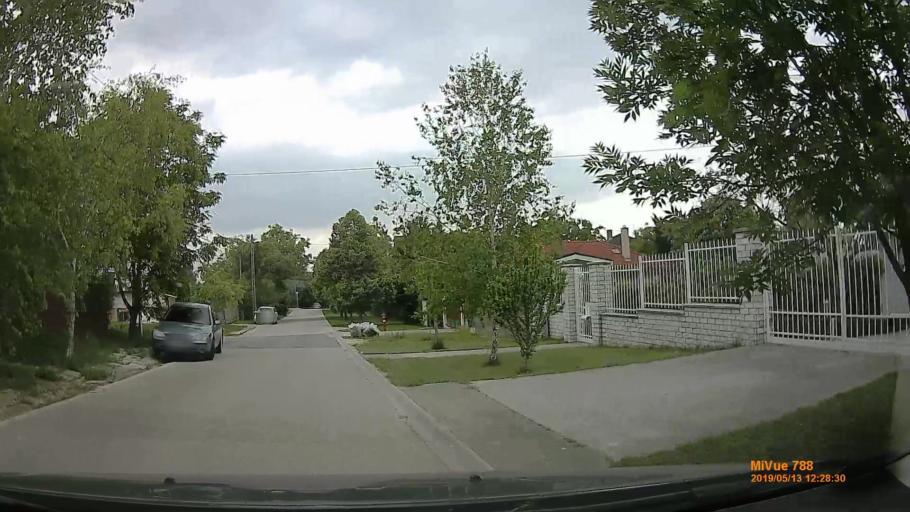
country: HU
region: Pest
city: Diosd
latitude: 47.4062
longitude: 18.9824
